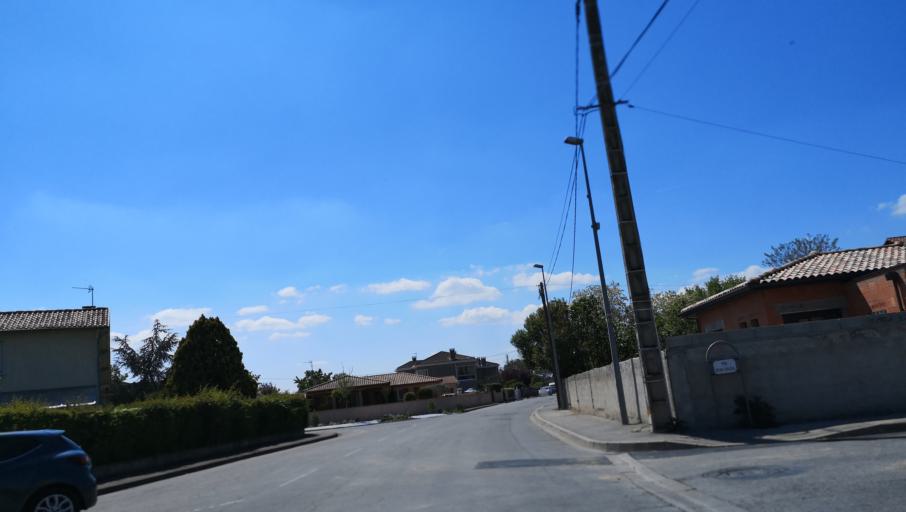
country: FR
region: Midi-Pyrenees
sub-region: Departement de la Haute-Garonne
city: Beauzelle
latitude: 43.6672
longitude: 1.3750
